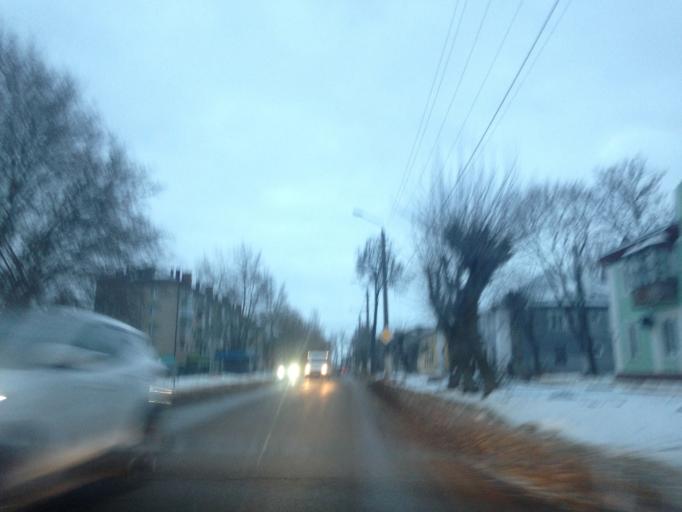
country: RU
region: Tula
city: Shchekino
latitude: 54.0002
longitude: 37.5270
